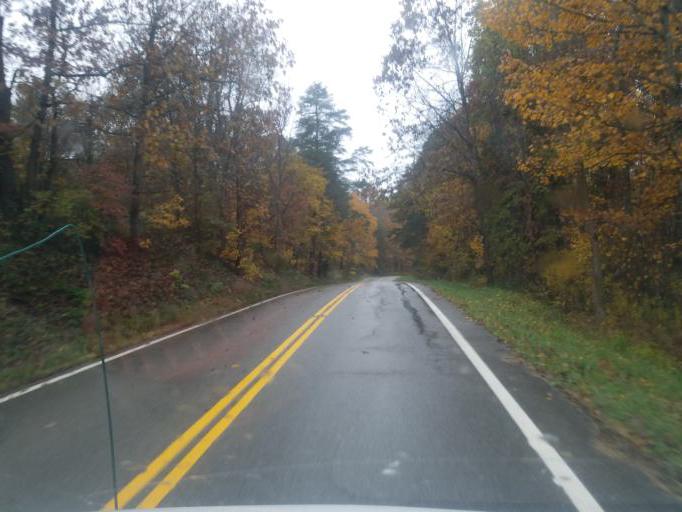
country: US
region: Ohio
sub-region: Washington County
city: Beverly
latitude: 39.4733
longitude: -81.7255
